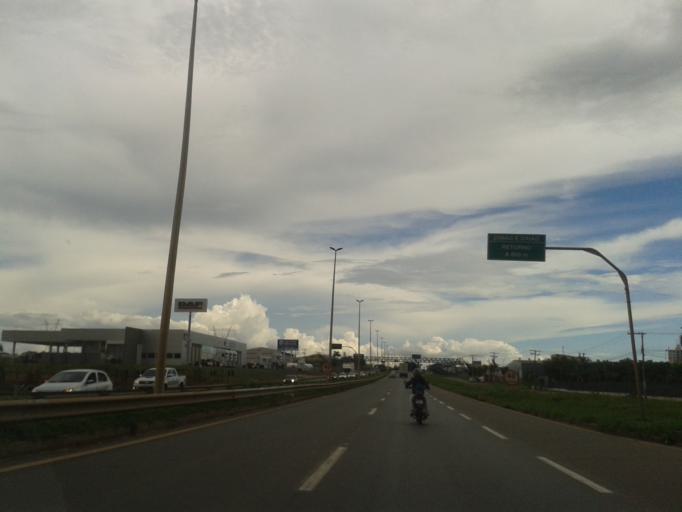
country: BR
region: Goias
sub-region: Aparecida De Goiania
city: Aparecida de Goiania
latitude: -16.8070
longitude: -49.2394
